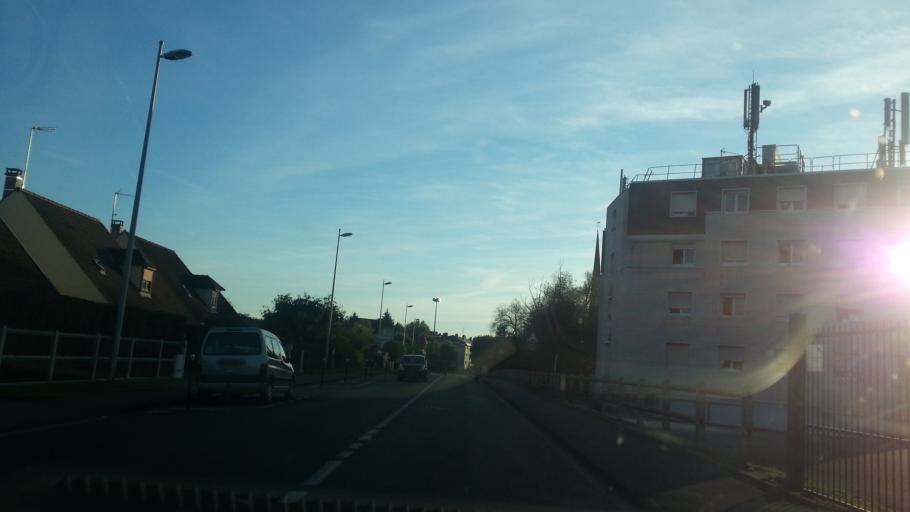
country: FR
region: Picardie
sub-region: Departement de l'Oise
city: Compiegne
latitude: 49.4059
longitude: 2.8243
